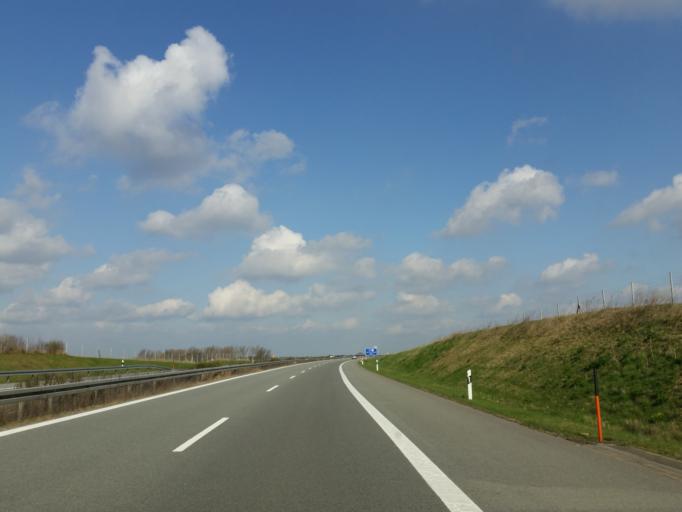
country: DE
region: Mecklenburg-Vorpommern
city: Neuenkirchen
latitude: 53.6062
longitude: 13.3737
